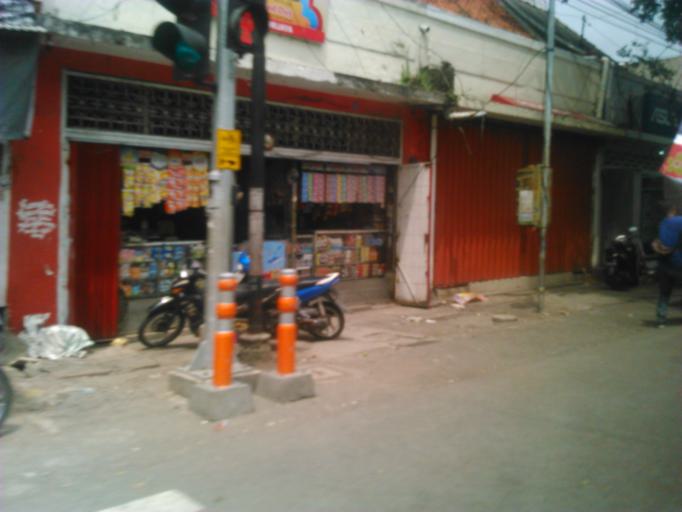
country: ID
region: East Java
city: Gubengairlangga
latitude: -7.2697
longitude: 112.7288
